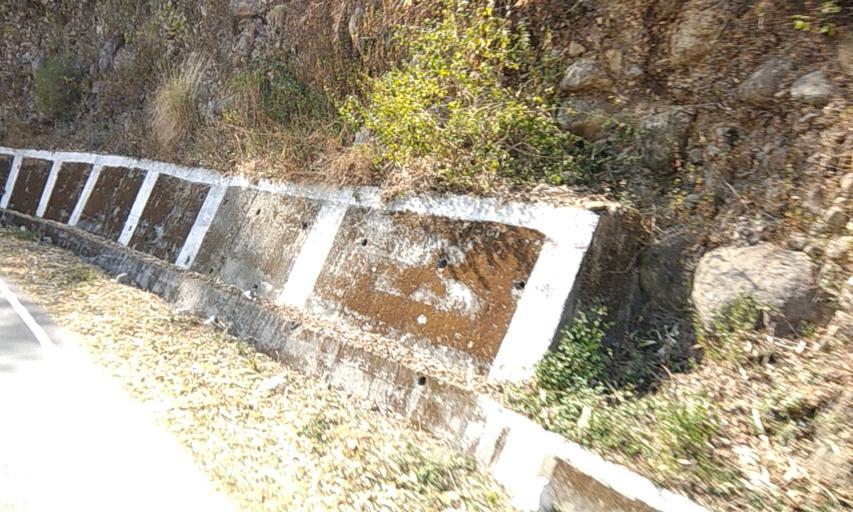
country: IN
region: Himachal Pradesh
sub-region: Kangra
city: Dharmsala
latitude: 32.1608
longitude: 76.4045
